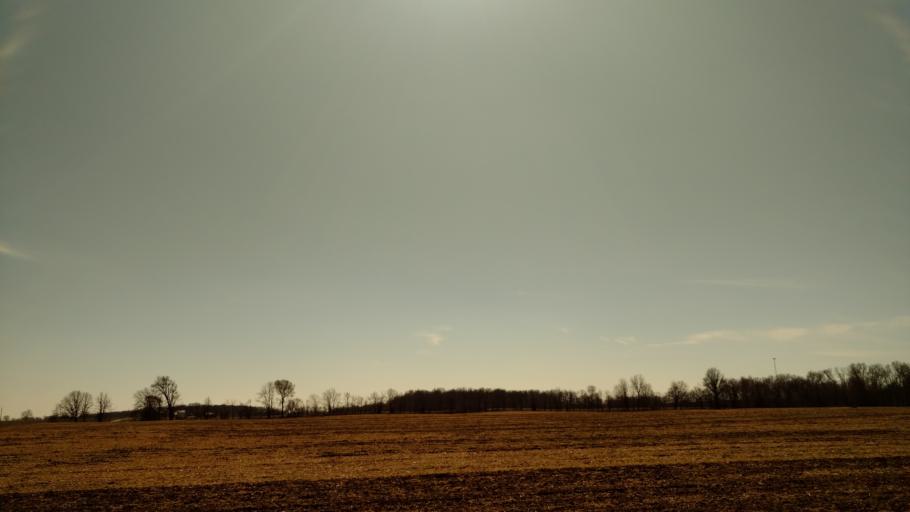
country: US
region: Ohio
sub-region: Union County
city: Richwood
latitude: 40.5272
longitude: -83.3151
